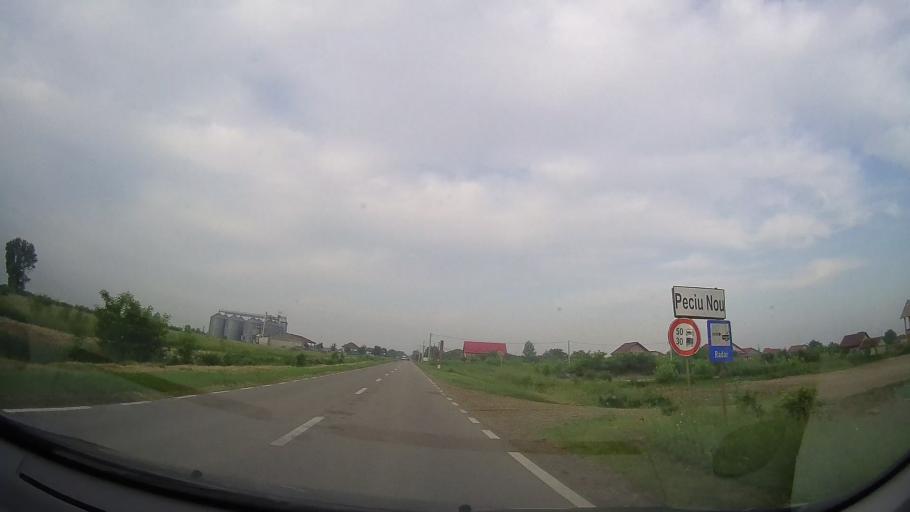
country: RO
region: Timis
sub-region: Comuna Peciu Nou
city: Peciu Nou
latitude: 45.6149
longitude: 21.0741
